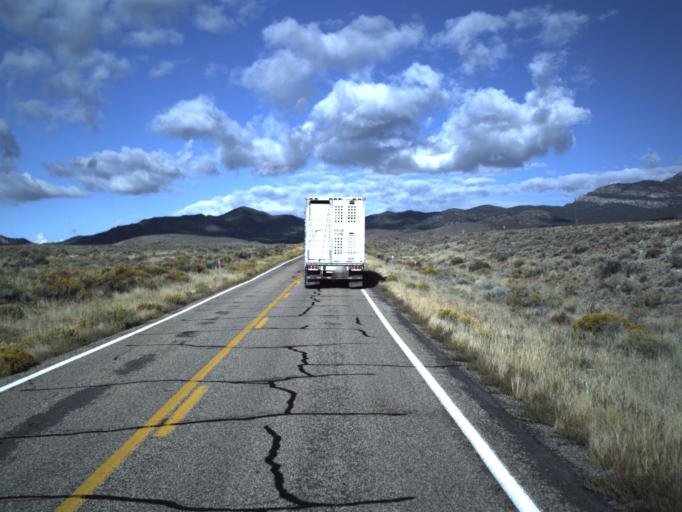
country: US
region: Utah
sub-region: Beaver County
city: Milford
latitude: 38.4494
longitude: -113.1948
